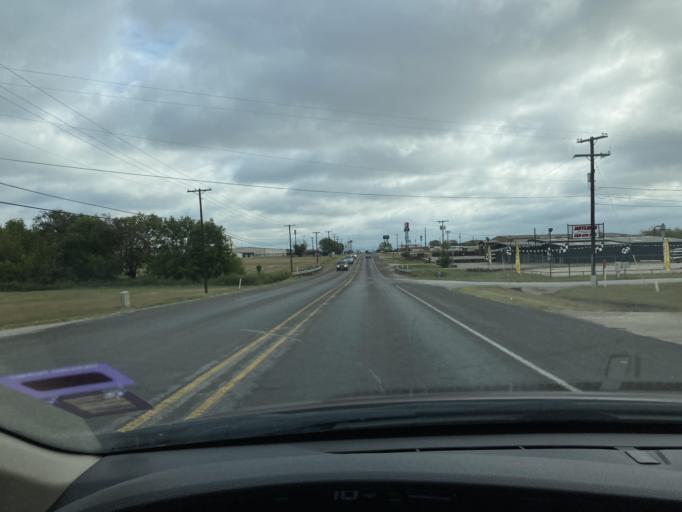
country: US
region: Texas
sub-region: Navarro County
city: Corsicana
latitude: 32.0805
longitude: -96.4498
